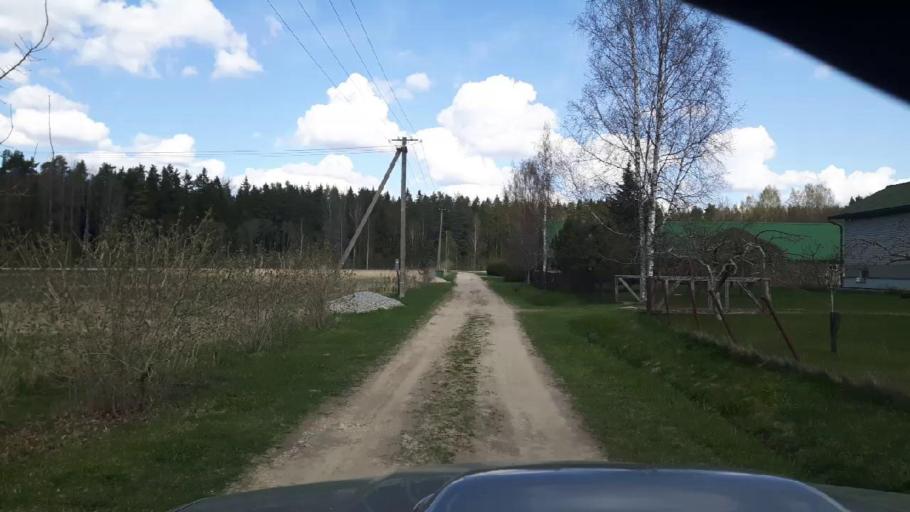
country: EE
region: Paernumaa
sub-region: Tootsi vald
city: Tootsi
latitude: 58.5012
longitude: 24.9301
